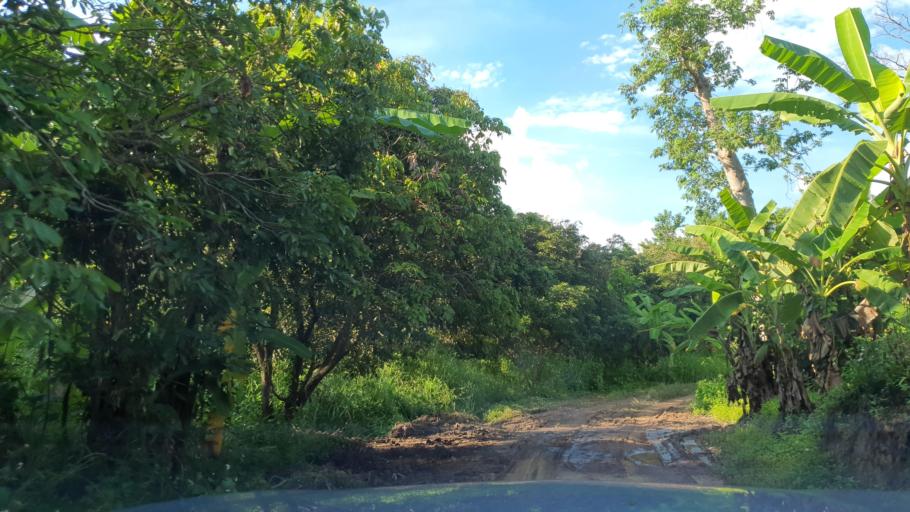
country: TH
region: Chiang Mai
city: Hang Dong
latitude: 18.7186
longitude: 98.8538
